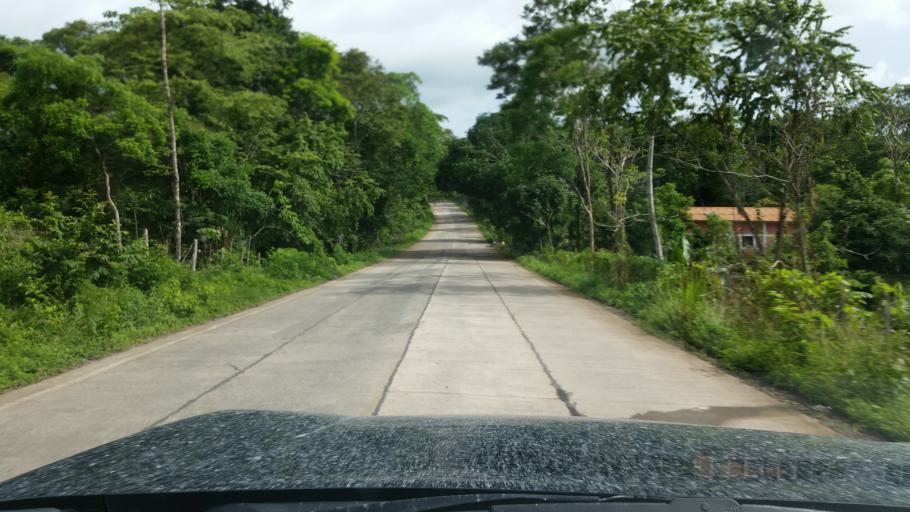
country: NI
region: Atlantico Norte (RAAN)
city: Siuna
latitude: 13.5614
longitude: -84.8175
